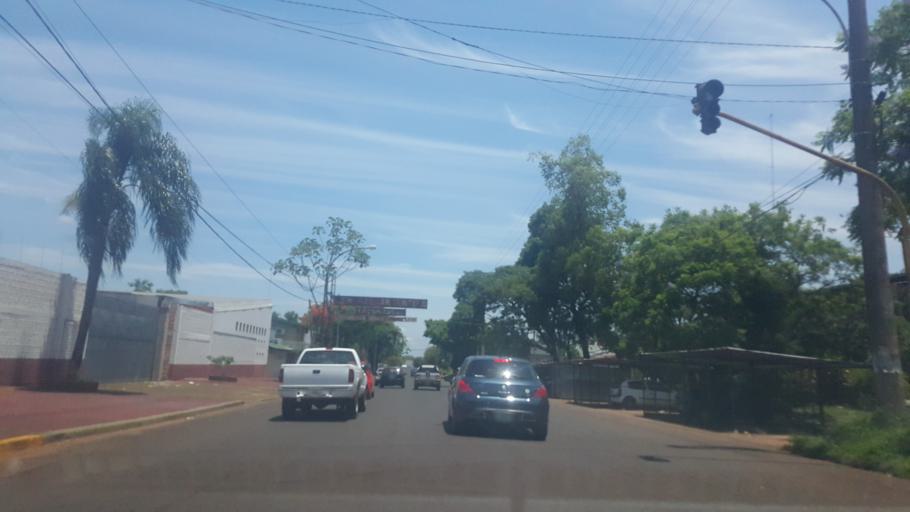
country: AR
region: Misiones
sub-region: Departamento de Capital
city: Posadas
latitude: -27.3973
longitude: -55.9055
